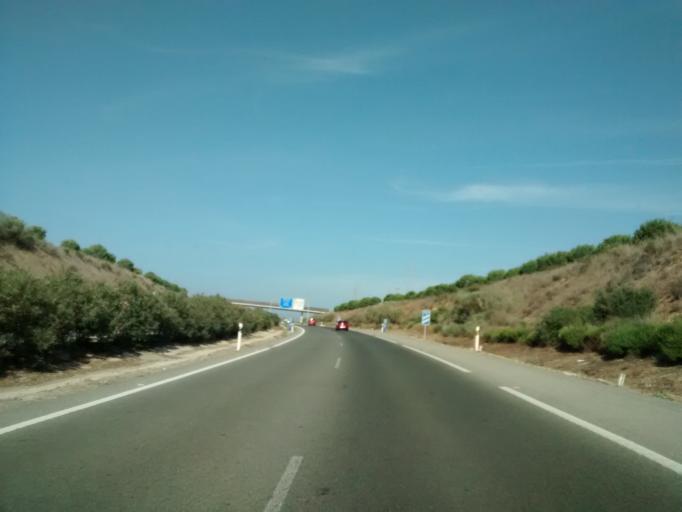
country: ES
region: Andalusia
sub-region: Provincia de Cadiz
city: Conil de la Frontera
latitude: 36.3449
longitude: -6.0545
